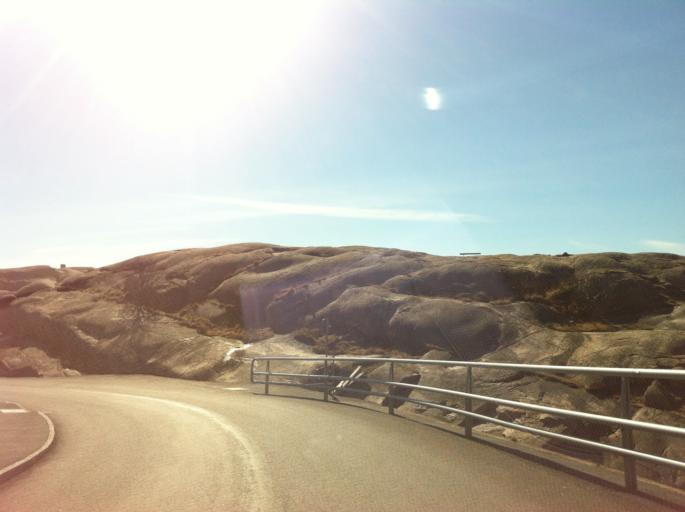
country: SE
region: Vaestra Goetaland
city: Smoegen
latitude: 58.3550
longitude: 11.2226
